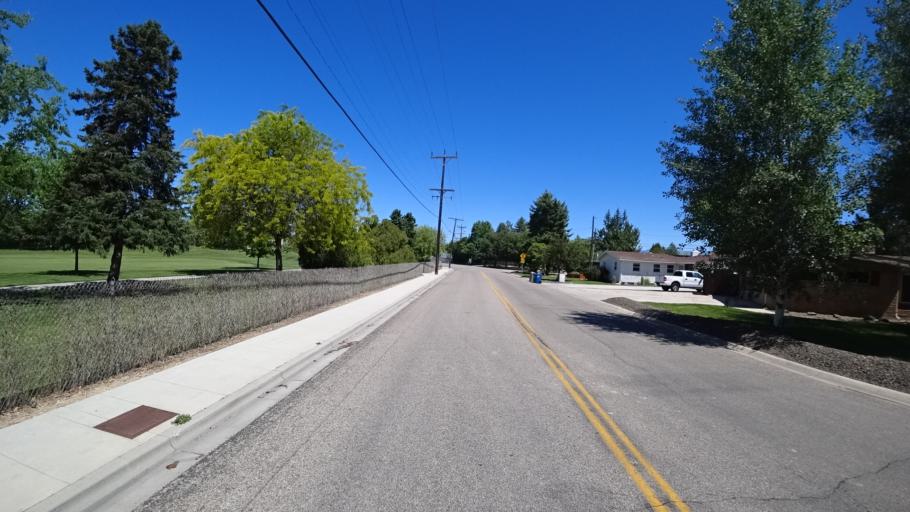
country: US
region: Idaho
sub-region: Ada County
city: Garden City
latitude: 43.5810
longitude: -116.2336
